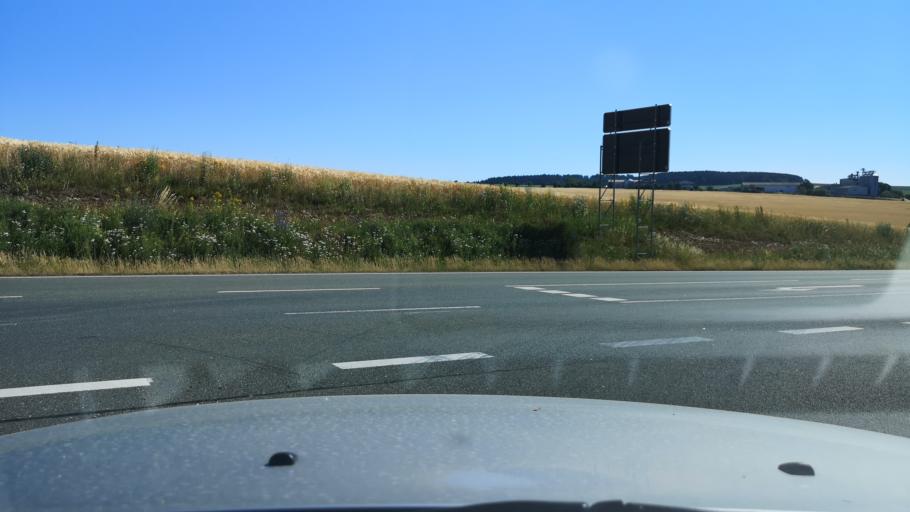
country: DE
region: Thuringia
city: Birkenhugel
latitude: 50.4445
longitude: 11.7580
